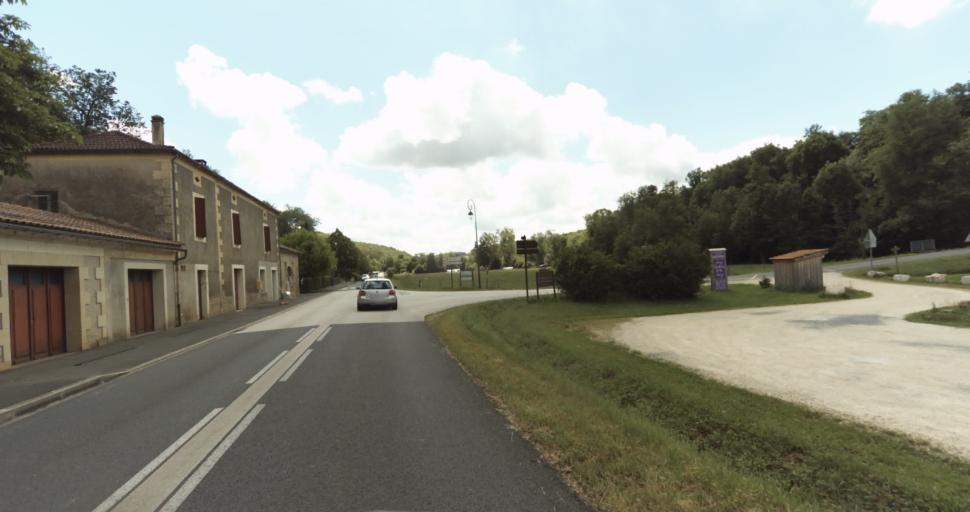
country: FR
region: Aquitaine
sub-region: Departement de la Dordogne
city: Lalinde
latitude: 44.8049
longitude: 0.7304
